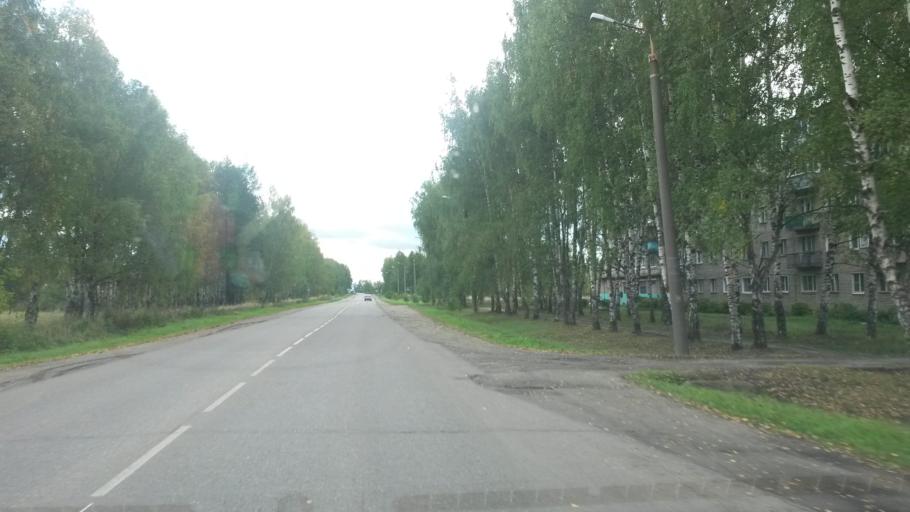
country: RU
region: Ivanovo
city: Zavolzhsk
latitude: 57.4713
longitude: 42.1584
